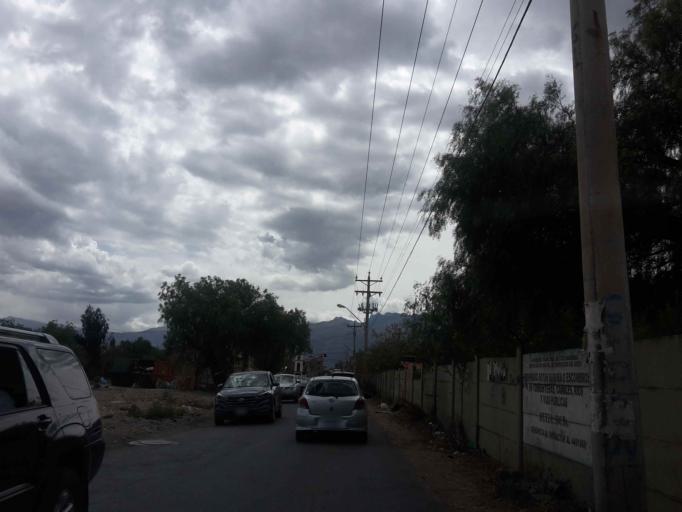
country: BO
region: Cochabamba
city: Cochabamba
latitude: -17.3494
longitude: -66.1879
